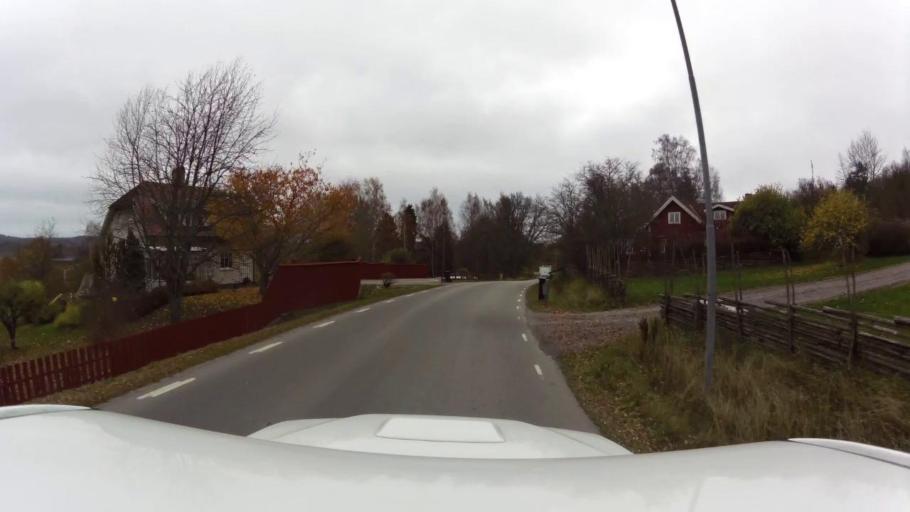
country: SE
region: OEstergoetland
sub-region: Kinda Kommun
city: Rimforsa
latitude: 58.1417
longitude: 15.6738
